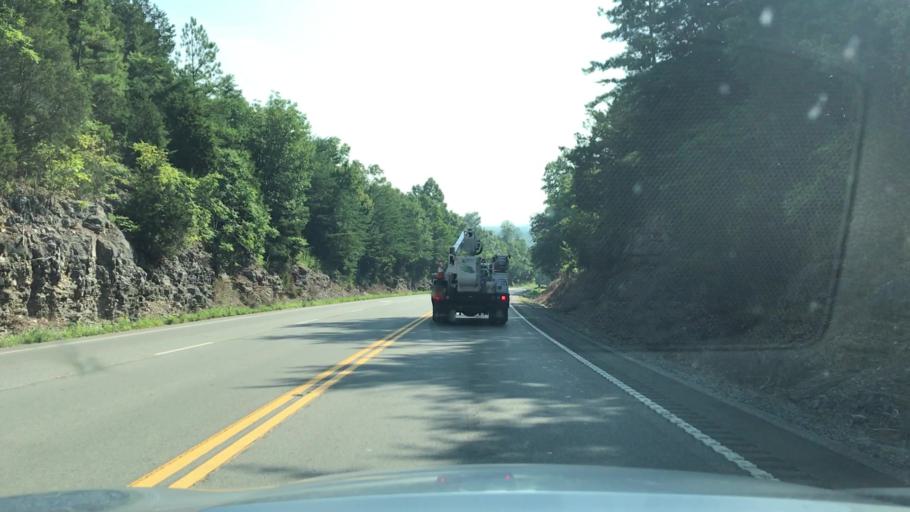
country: US
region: Tennessee
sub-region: Overton County
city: Livingston
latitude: 36.4371
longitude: -85.2731
